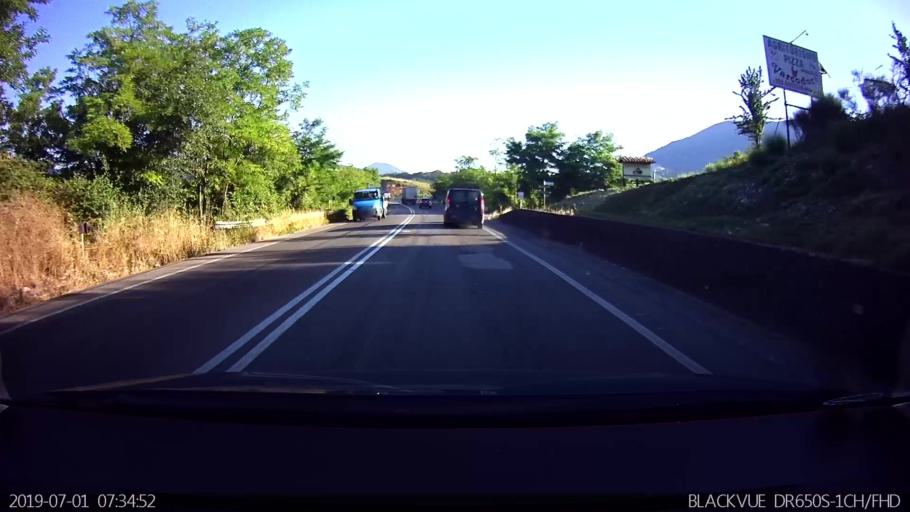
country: IT
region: Latium
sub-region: Provincia di Latina
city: Prossedi
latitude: 41.5198
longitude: 13.2729
